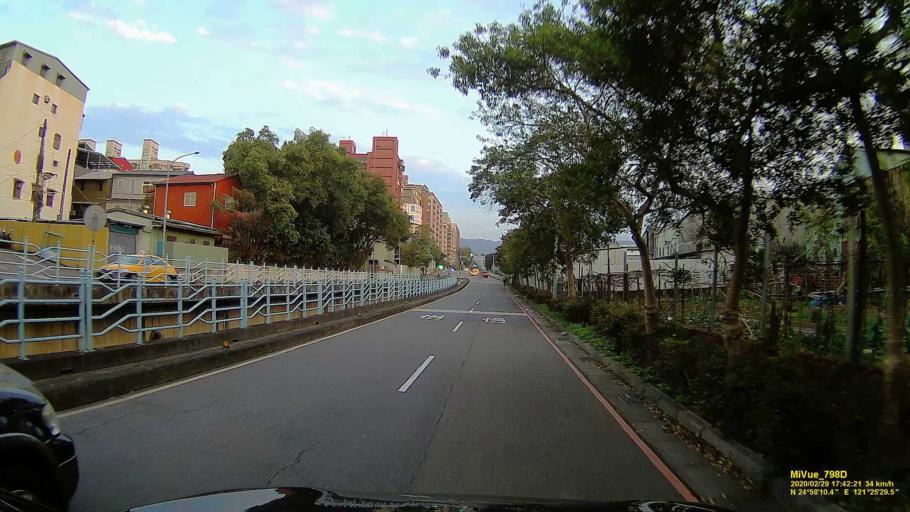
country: TW
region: Taipei
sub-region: Taipei
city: Banqiao
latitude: 24.9860
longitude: 121.4250
